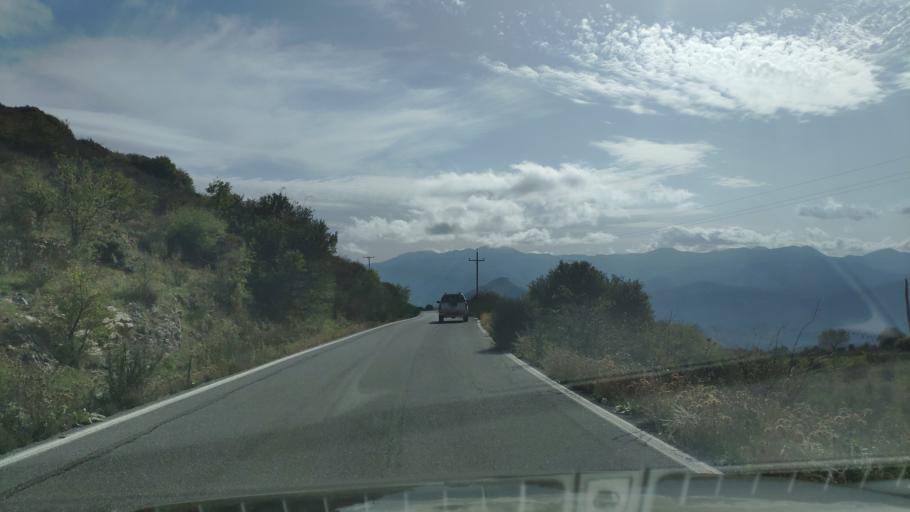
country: GR
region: Peloponnese
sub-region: Nomos Arkadias
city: Dimitsana
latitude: 37.5771
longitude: 22.0186
